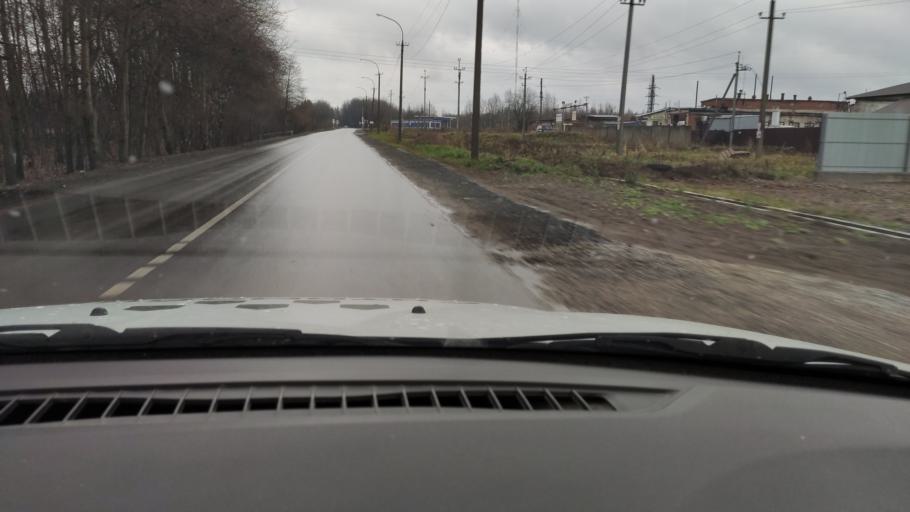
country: RU
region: Perm
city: Sylva
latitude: 58.0284
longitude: 56.7397
